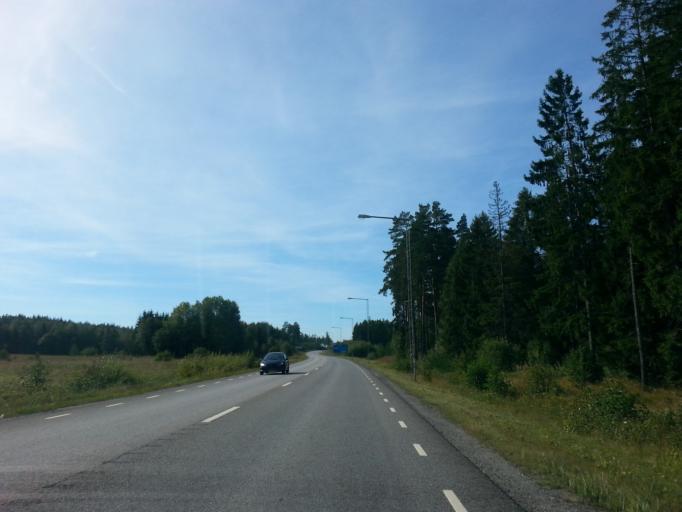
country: SE
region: Stockholm
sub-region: Sigtuna Kommun
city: Rosersberg
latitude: 59.6323
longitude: 17.9298
